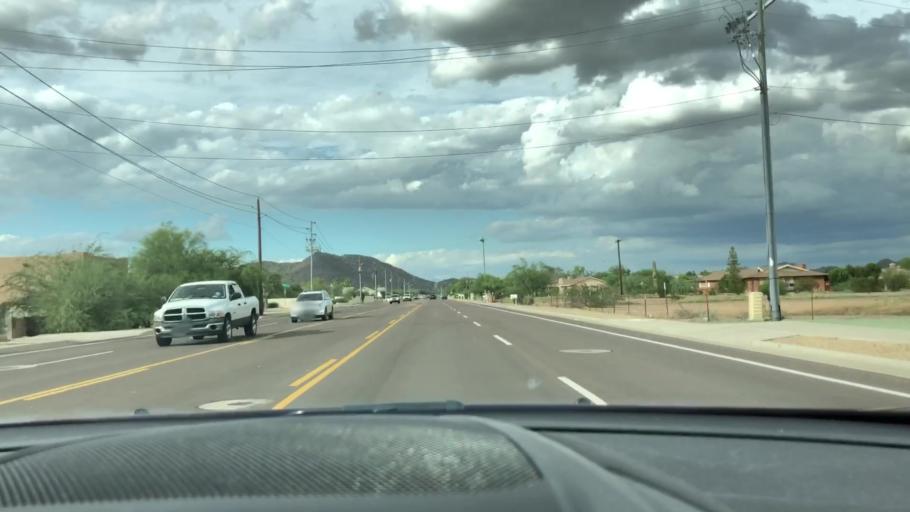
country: US
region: Arizona
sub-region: Maricopa County
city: Sun City
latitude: 33.6897
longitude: -112.2376
